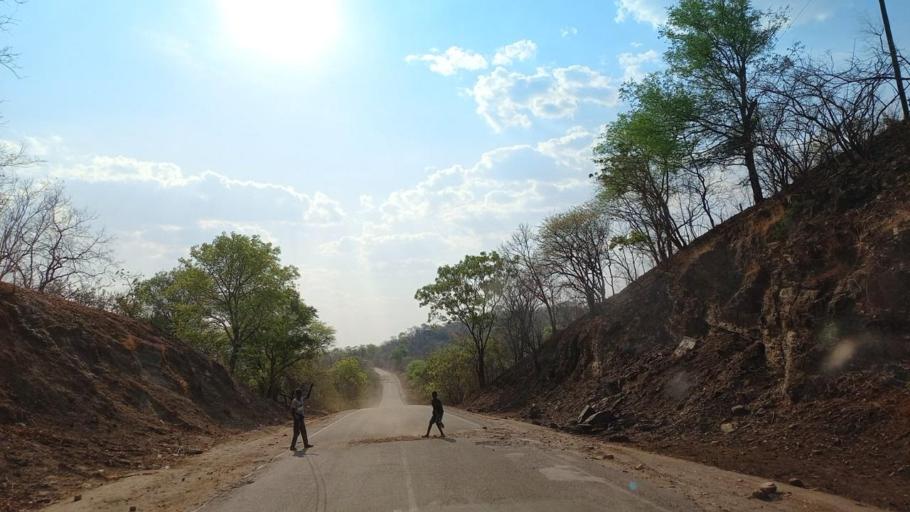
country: ZM
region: Lusaka
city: Luangwa
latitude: -14.9827
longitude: 30.1667
